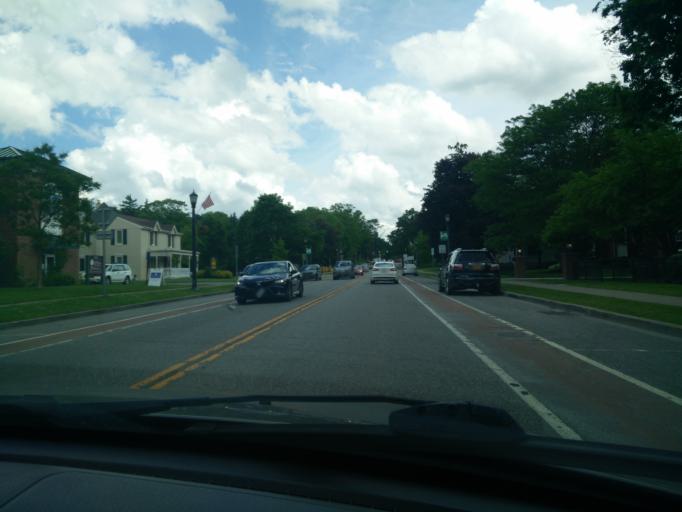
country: US
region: New York
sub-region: Erie County
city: East Aurora
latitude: 42.7680
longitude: -78.6250
